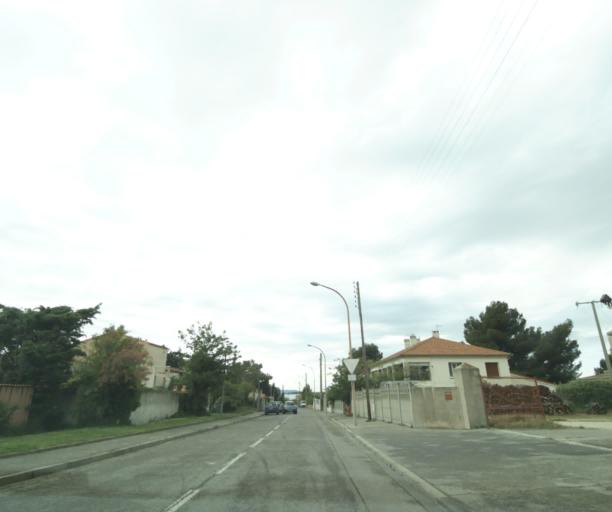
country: FR
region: Provence-Alpes-Cote d'Azur
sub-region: Departement des Bouches-du-Rhone
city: Rognac
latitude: 43.4836
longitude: 5.2266
